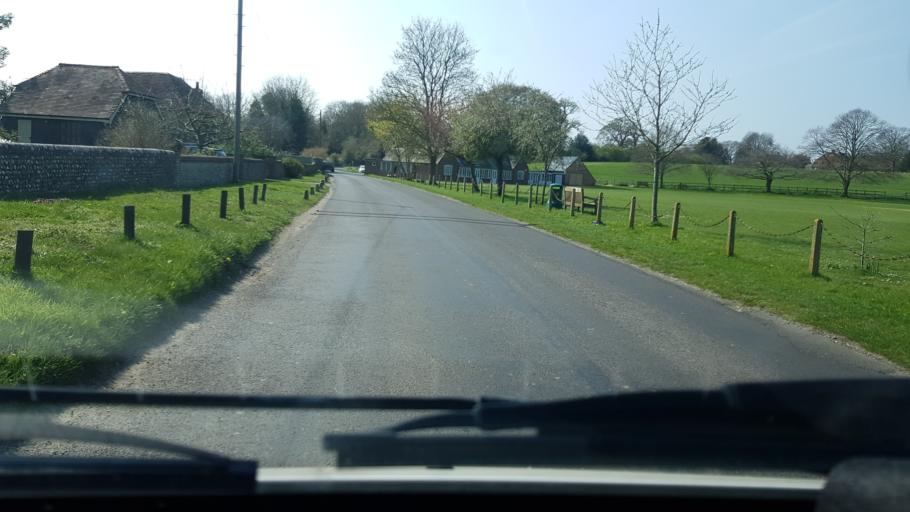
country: GB
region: England
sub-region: West Sussex
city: Chichester
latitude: 50.8681
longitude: -0.7782
